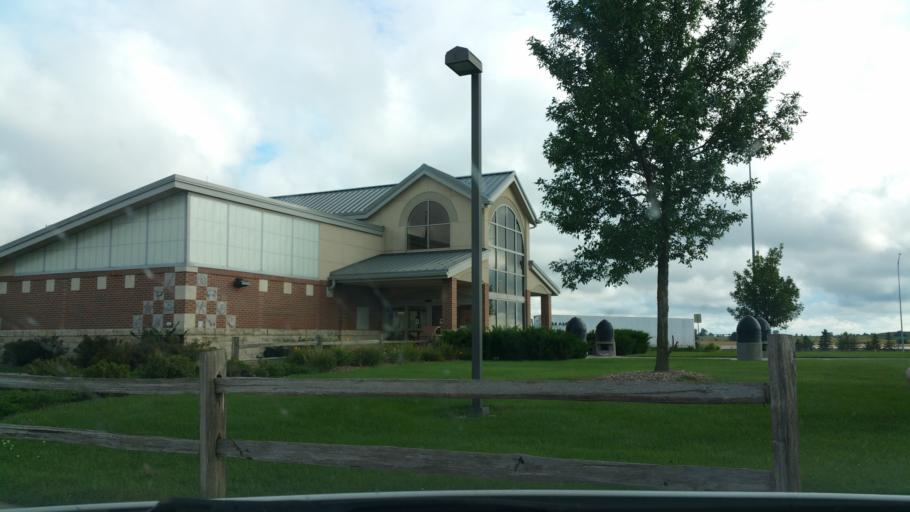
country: US
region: Iowa
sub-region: Franklin County
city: Oakland
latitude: 42.6725
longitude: -93.4604
